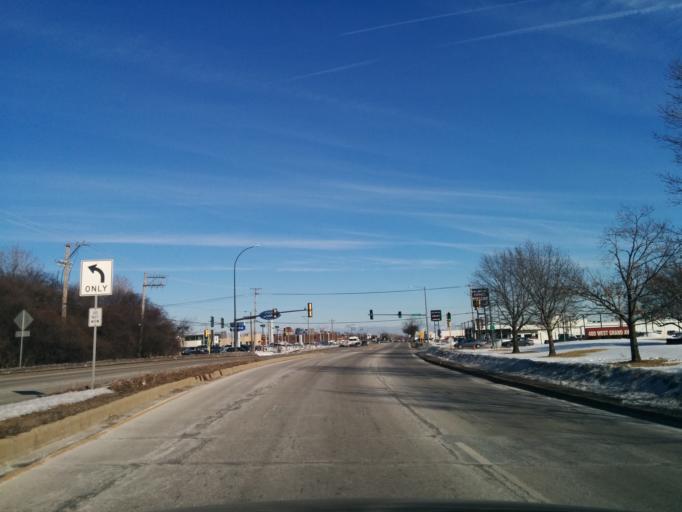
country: US
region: Illinois
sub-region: DuPage County
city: Bensenville
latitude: 41.9306
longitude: -87.9547
